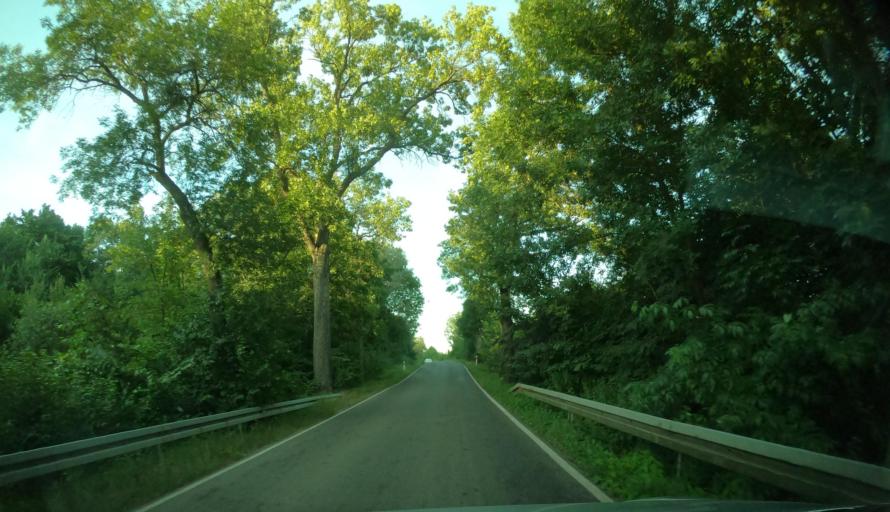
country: PL
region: Kujawsko-Pomorskie
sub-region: Bydgoszcz
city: Fordon
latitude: 53.2260
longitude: 18.1951
